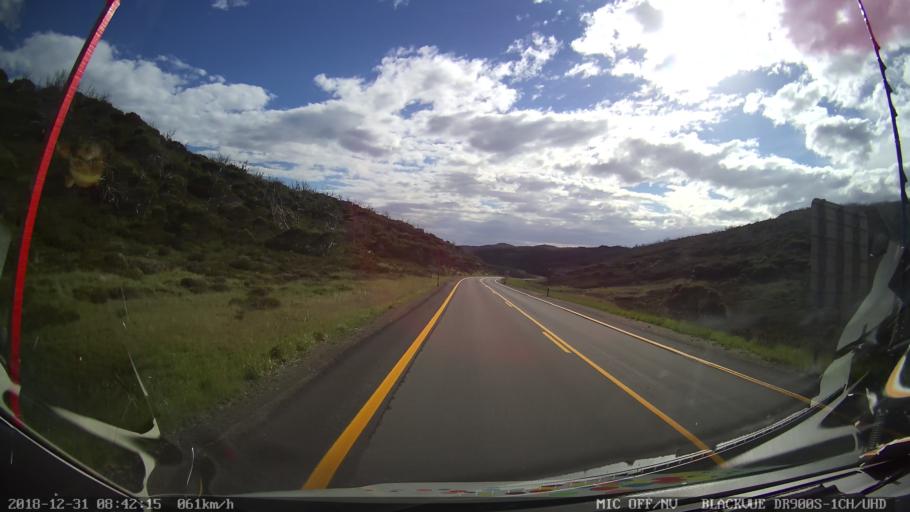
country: AU
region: New South Wales
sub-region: Snowy River
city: Jindabyne
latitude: -36.3943
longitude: 148.4300
